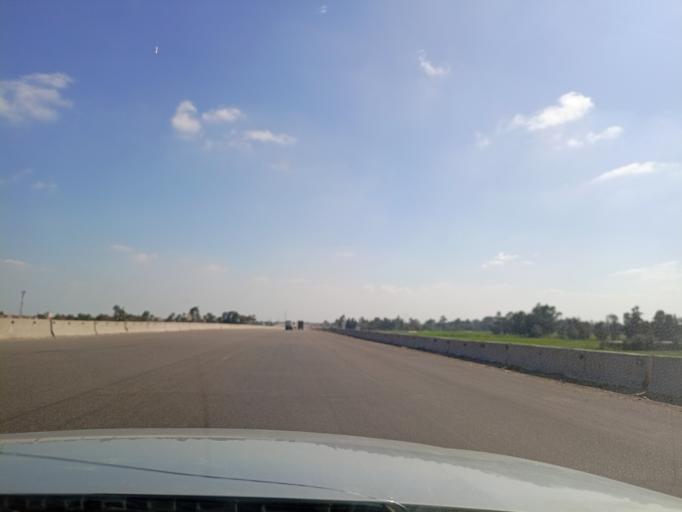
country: EG
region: Eastern Province
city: Mashtul as Suq
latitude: 30.4644
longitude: 31.3159
